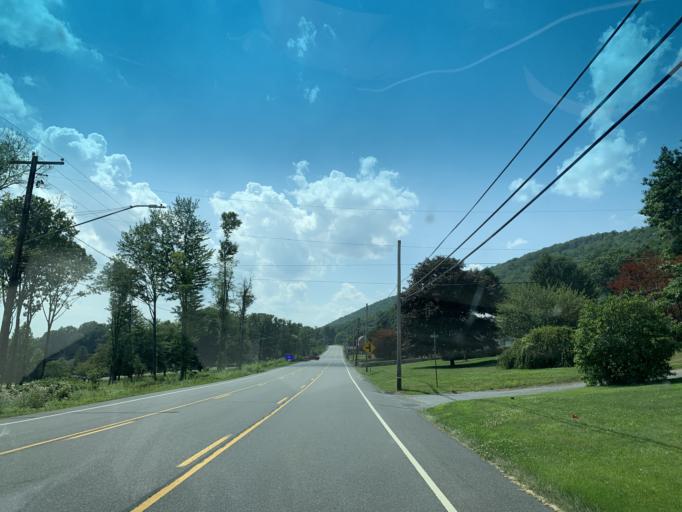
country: US
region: Pennsylvania
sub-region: Schuylkill County
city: Girardville
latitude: 40.7769
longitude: -76.2959
